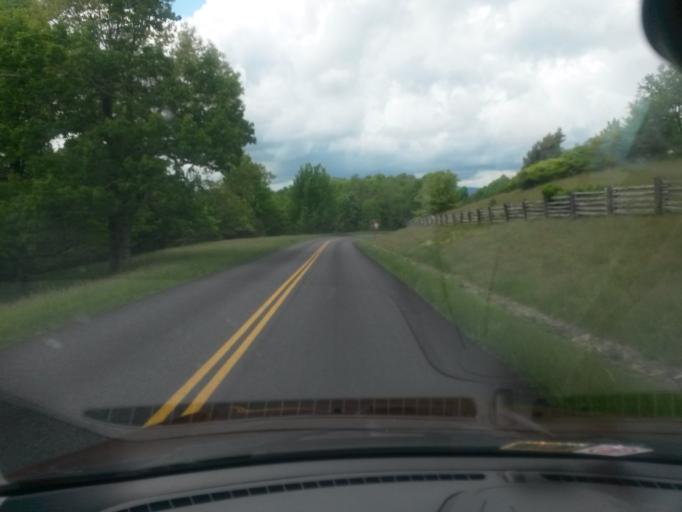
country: US
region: Virginia
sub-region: Floyd County
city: Floyd
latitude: 36.8289
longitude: -80.3457
